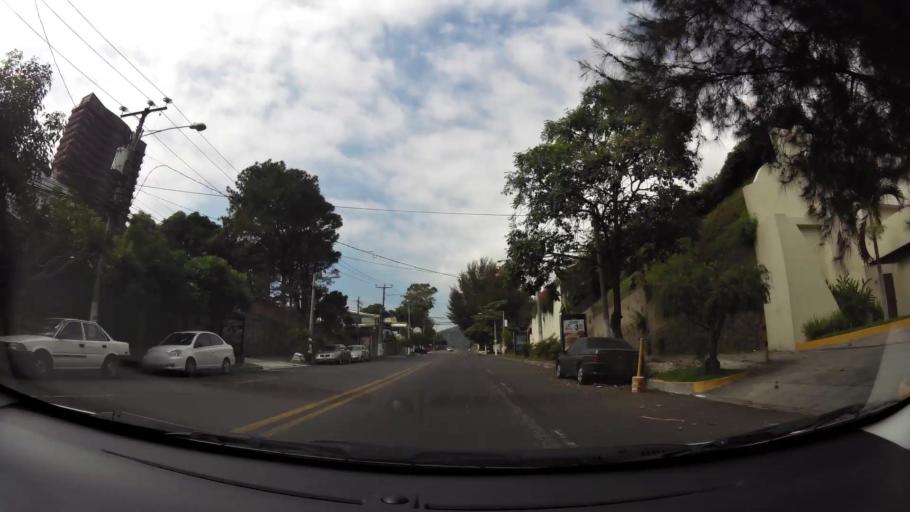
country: SV
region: La Libertad
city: Santa Tecla
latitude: 13.7041
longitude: -89.2545
